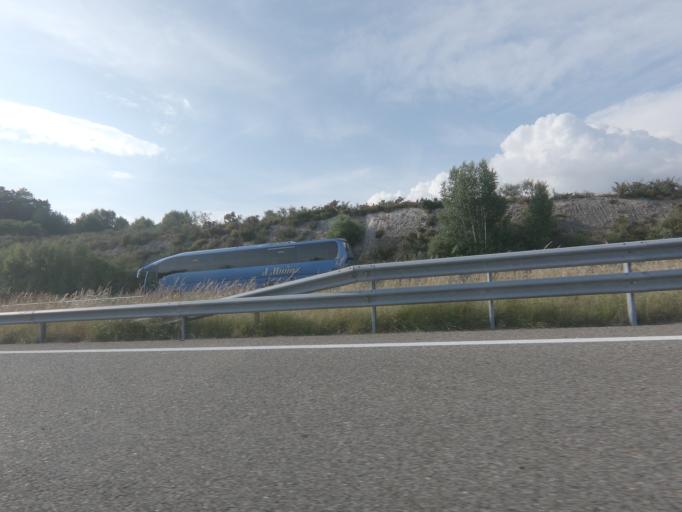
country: ES
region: Galicia
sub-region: Provincia de Ourense
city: Xinzo de Limia
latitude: 42.0642
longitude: -7.6895
